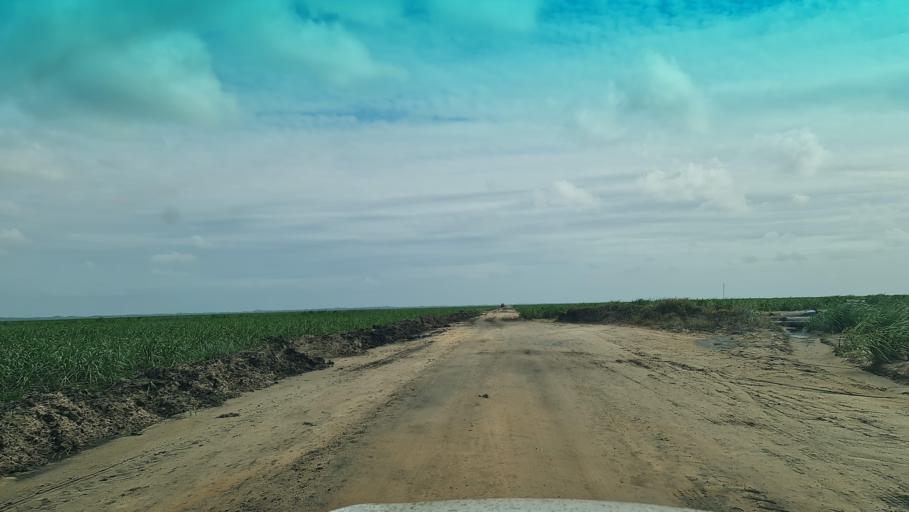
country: MZ
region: Maputo
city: Manhica
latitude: -25.4722
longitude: 32.8171
